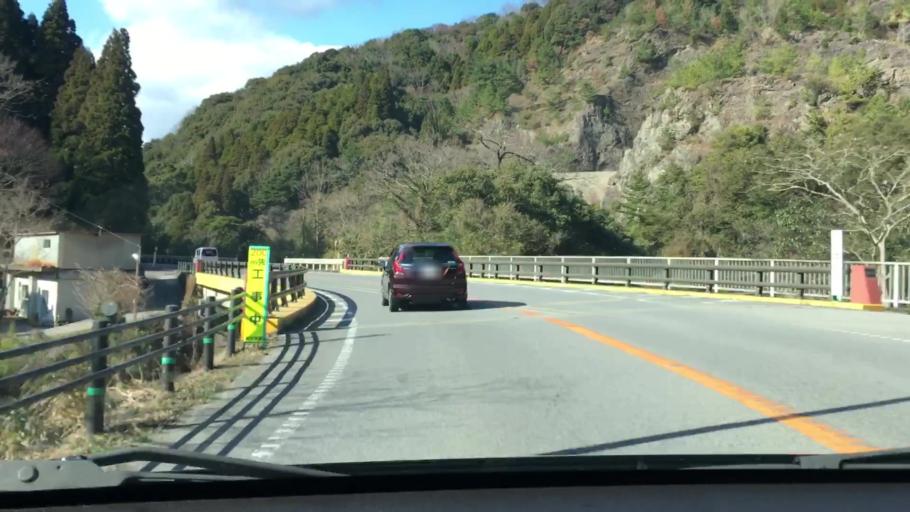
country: JP
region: Oita
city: Tsukumiura
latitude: 32.9969
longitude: 131.8201
